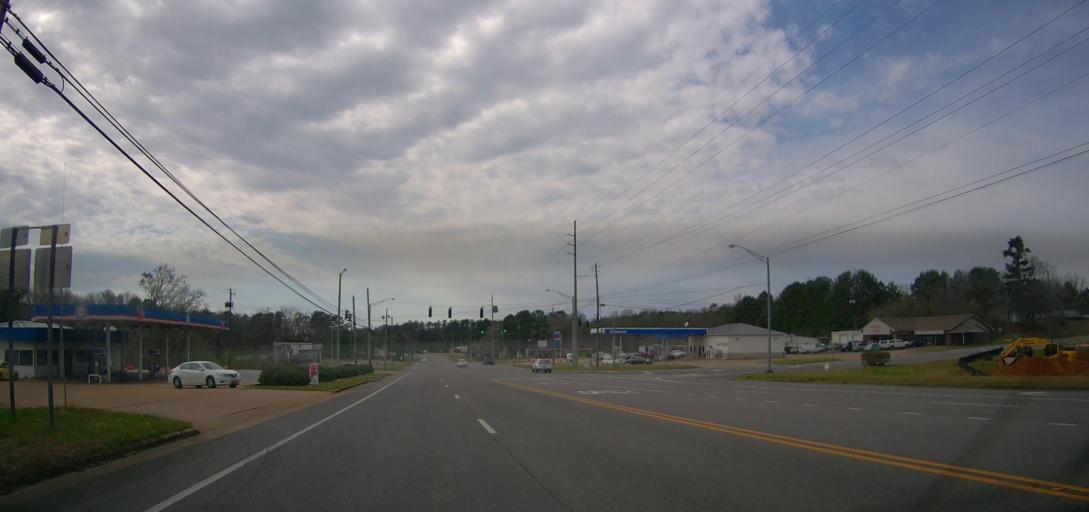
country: US
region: Alabama
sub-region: Marion County
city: Winfield
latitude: 33.9317
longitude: -87.7824
